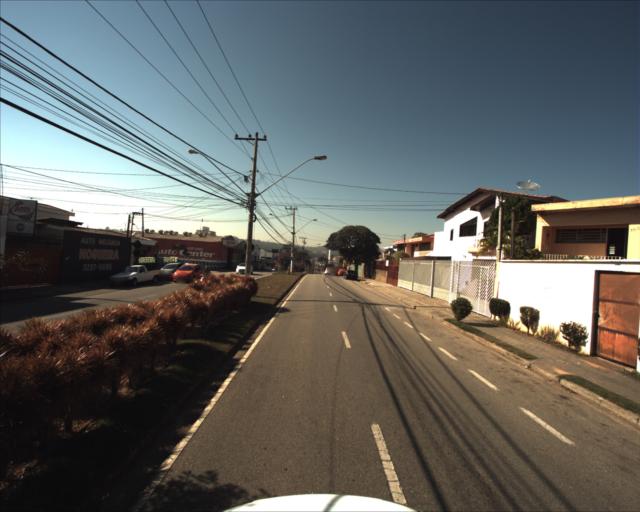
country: BR
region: Sao Paulo
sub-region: Sorocaba
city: Sorocaba
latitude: -23.5093
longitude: -47.4378
